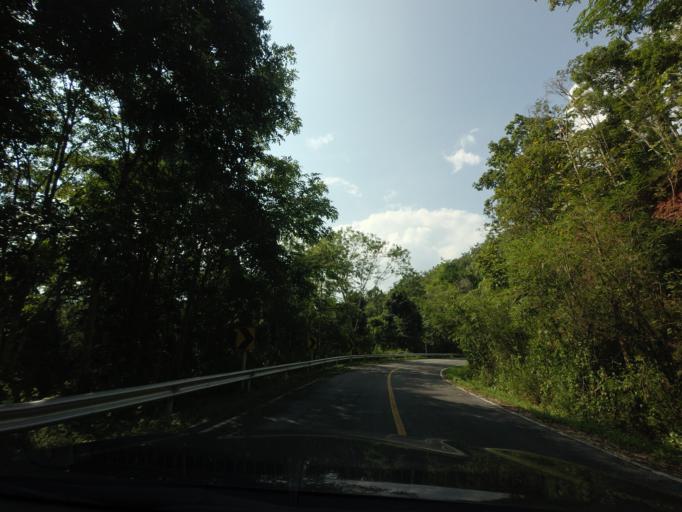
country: TH
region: Uttaradit
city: Ban Khok
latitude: 18.2481
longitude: 101.0011
